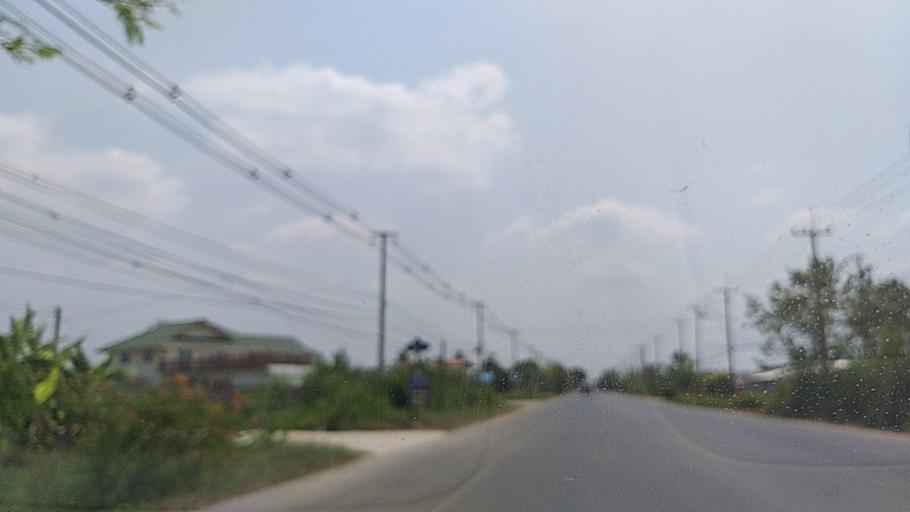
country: TH
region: Chachoengsao
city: Chachoengsao
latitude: 13.7556
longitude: 101.0753
